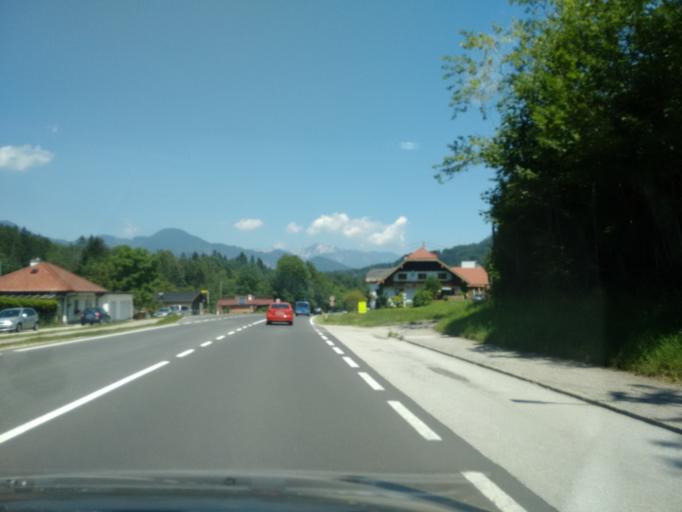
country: AT
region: Upper Austria
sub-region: Politischer Bezirk Gmunden
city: Bad Ischl
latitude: 47.6797
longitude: 13.6190
